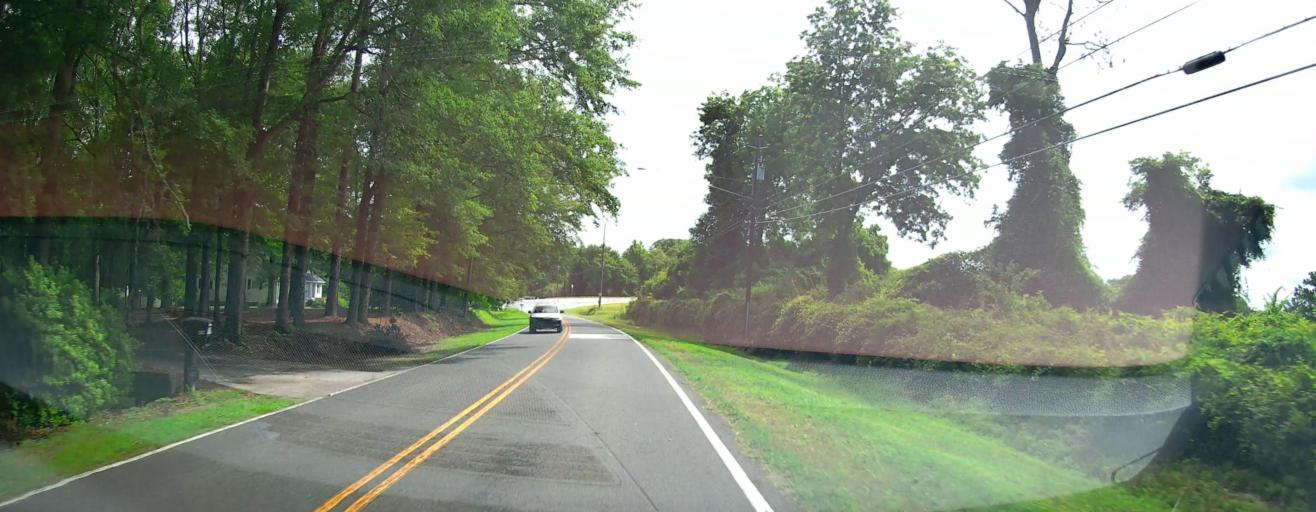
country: US
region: Georgia
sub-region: Peach County
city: Byron
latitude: 32.6499
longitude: -83.7648
